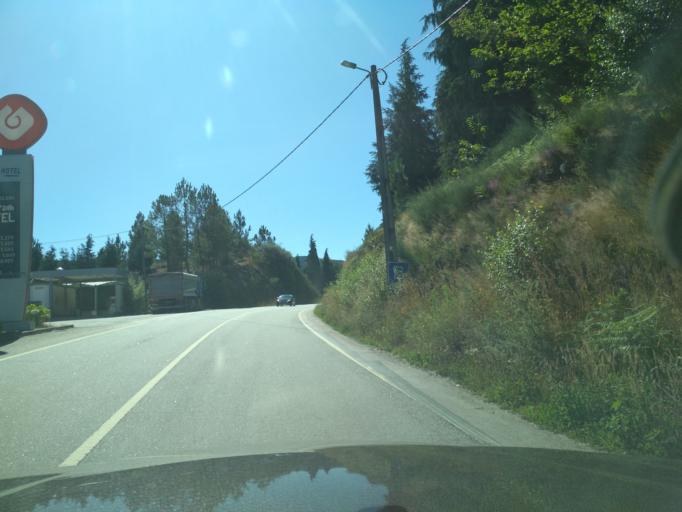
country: PT
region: Vila Real
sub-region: Ribeira de Pena
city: Ribeira de Pena
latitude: 41.5164
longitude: -7.8030
